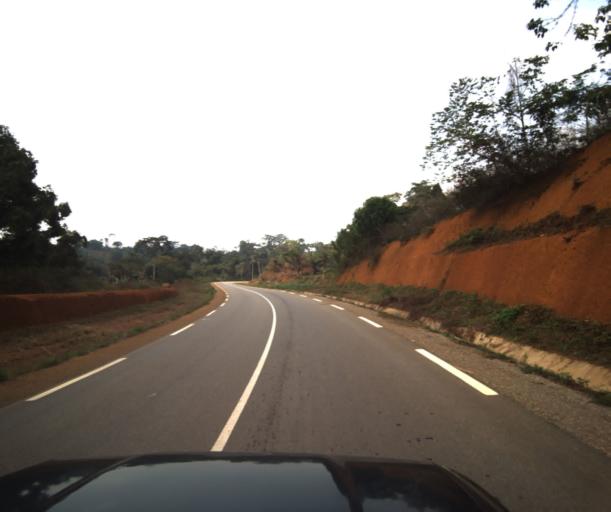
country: CM
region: Centre
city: Mbankomo
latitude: 3.6632
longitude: 11.3430
